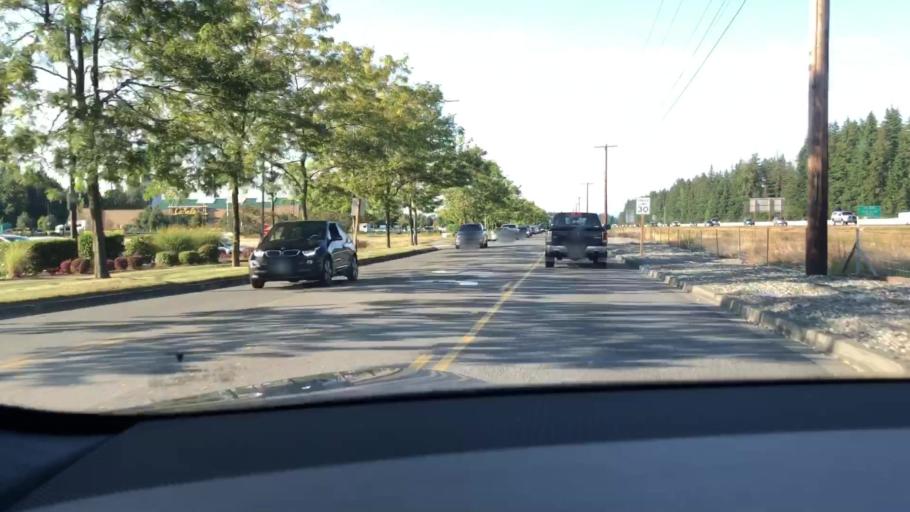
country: US
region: Washington
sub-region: Snohomish County
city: Marysville
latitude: 48.0814
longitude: -122.1855
